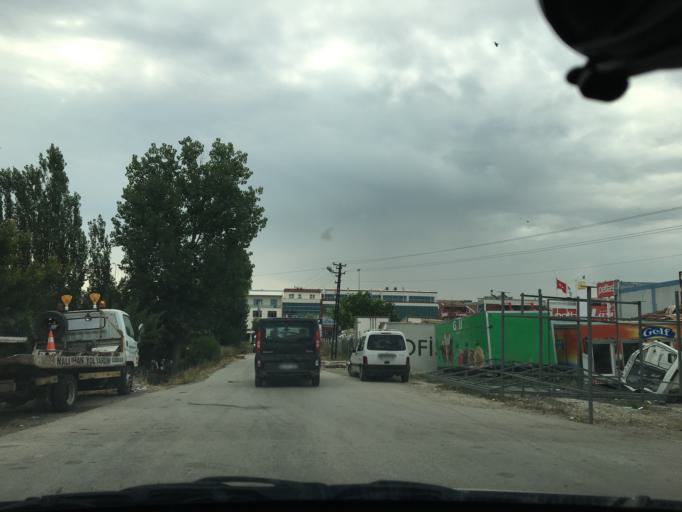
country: TR
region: Ankara
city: Batikent
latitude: 39.9352
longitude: 32.7116
